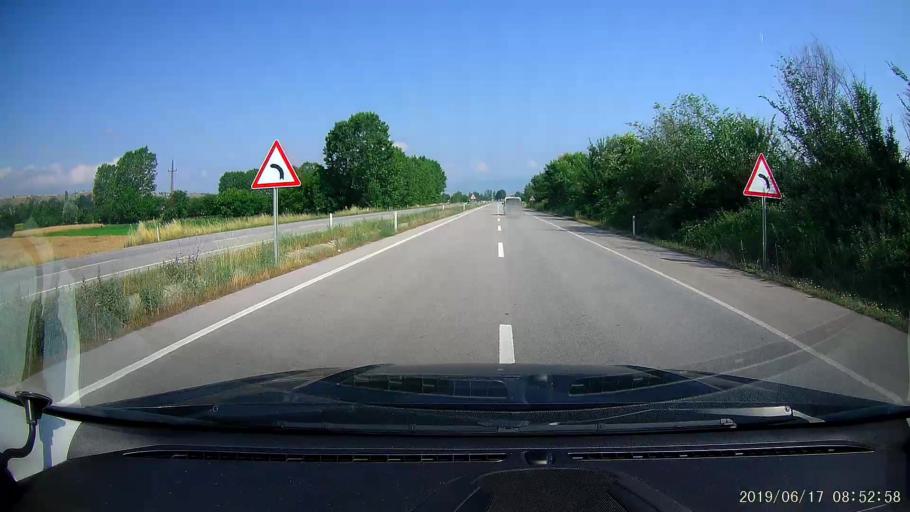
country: TR
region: Tokat
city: Erbaa
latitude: 40.7045
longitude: 36.4885
